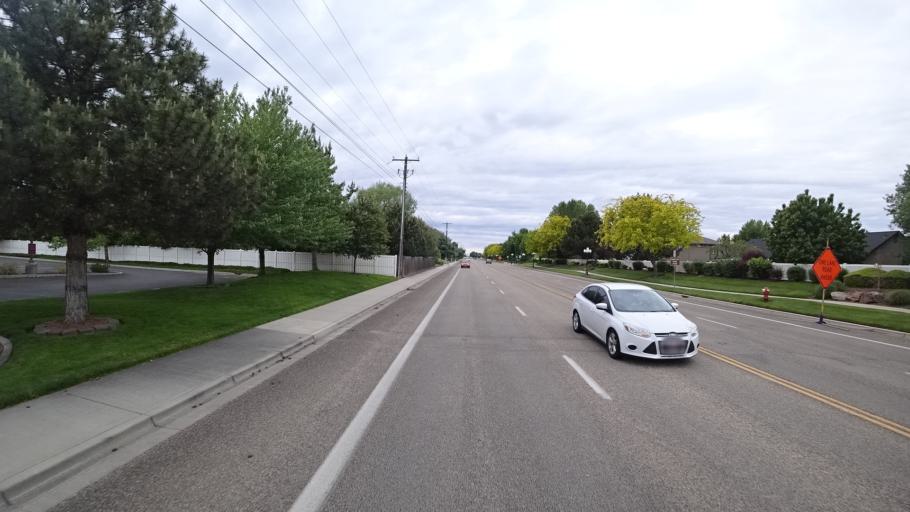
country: US
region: Idaho
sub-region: Ada County
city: Eagle
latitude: 43.6485
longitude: -116.3277
